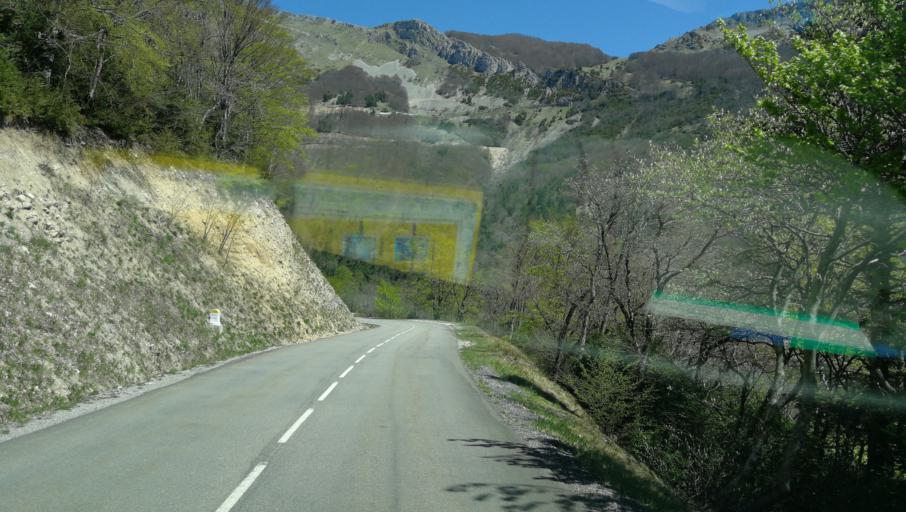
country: FR
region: Rhone-Alpes
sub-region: Departement de la Drome
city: Die
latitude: 44.8296
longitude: 5.3921
